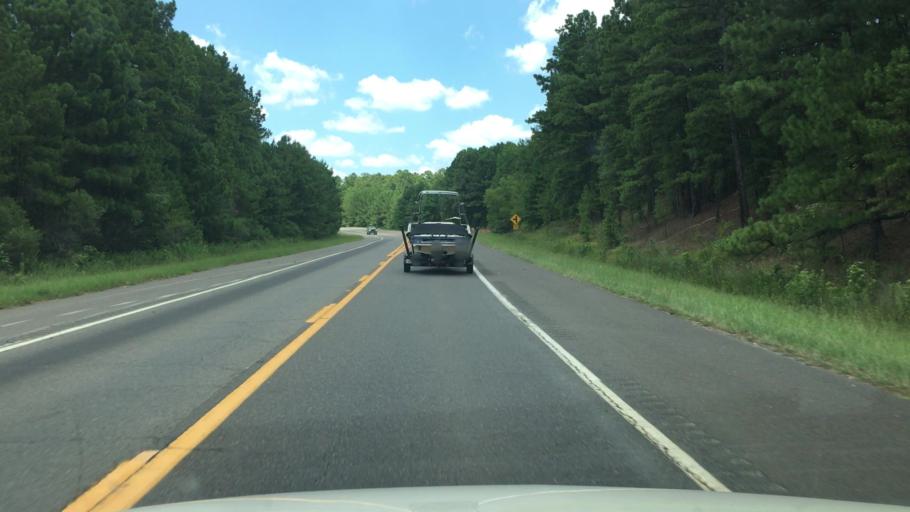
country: US
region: Arkansas
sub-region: Clark County
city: Arkadelphia
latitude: 34.2076
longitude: -93.0794
